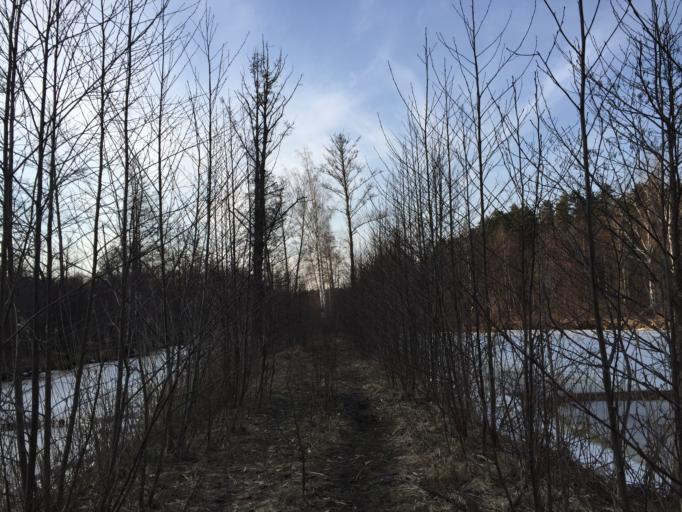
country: LV
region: Stopini
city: Ulbroka
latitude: 56.9594
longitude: 24.2841
